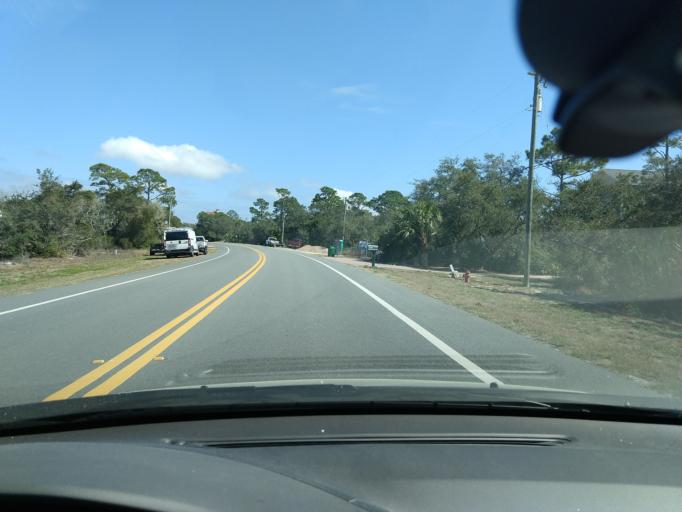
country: US
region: Florida
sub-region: Gulf County
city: Port Saint Joe
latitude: 29.6806
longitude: -85.2295
